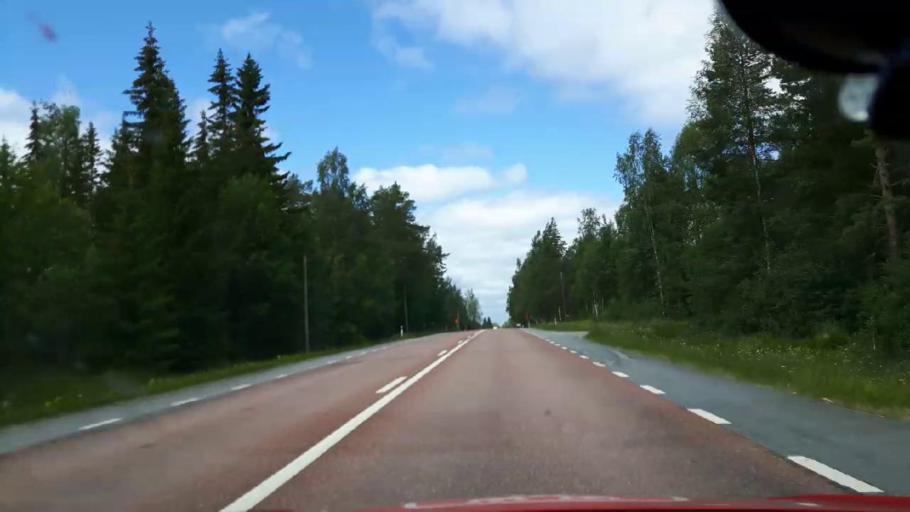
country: SE
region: Jaemtland
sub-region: Braecke Kommun
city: Braecke
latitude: 62.8238
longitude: 15.3257
